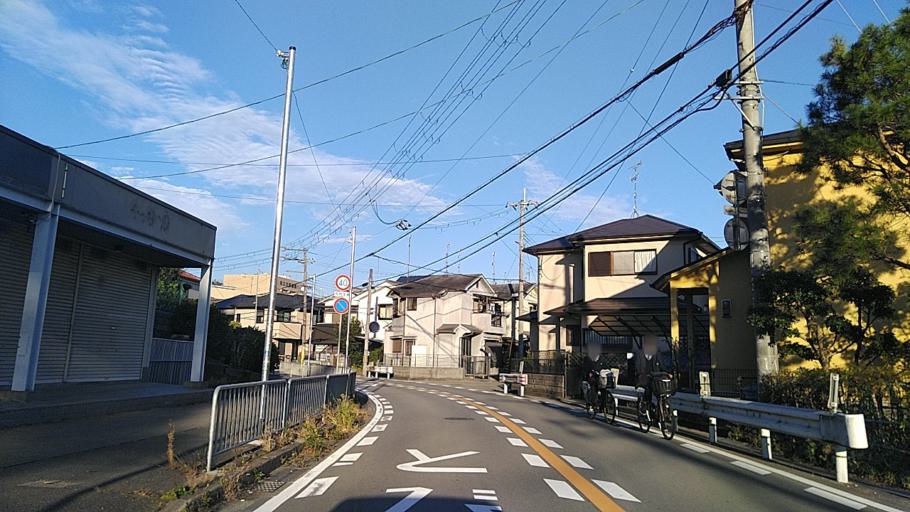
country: JP
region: Osaka
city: Ikeda
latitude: 34.8875
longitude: 135.4045
